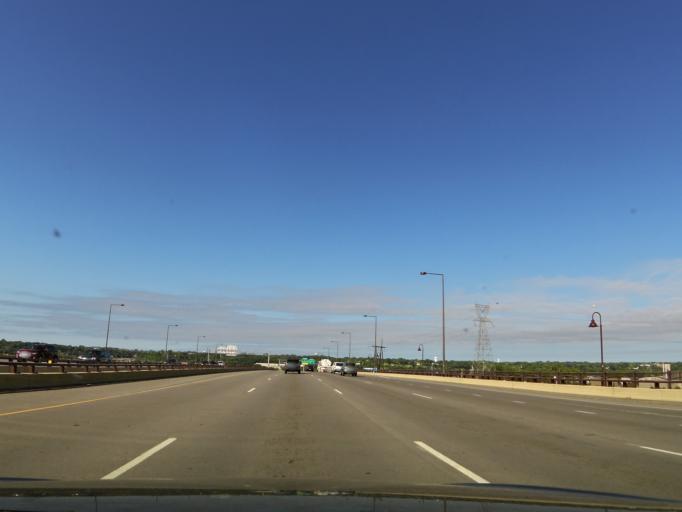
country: US
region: Minnesota
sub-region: Washington County
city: Newport
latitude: 44.8833
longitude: -93.0142
